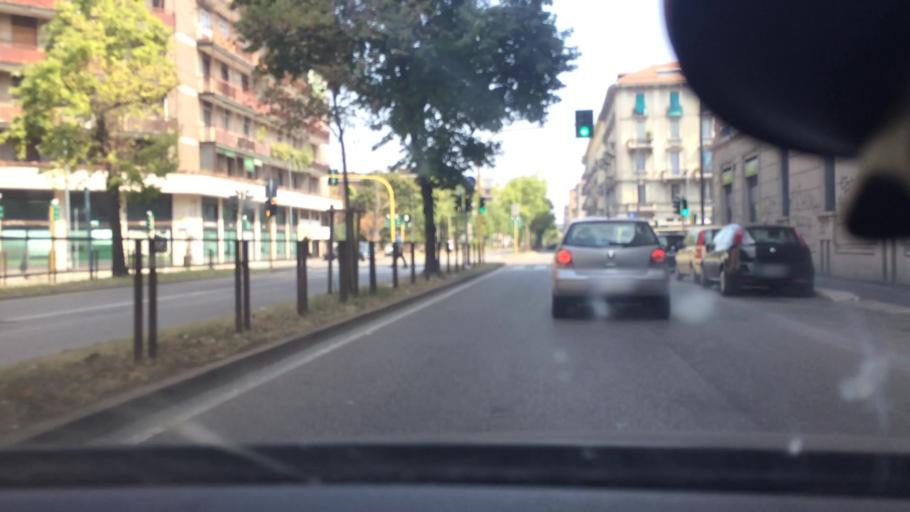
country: IT
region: Lombardy
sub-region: Citta metropolitana di Milano
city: Milano
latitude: 45.4941
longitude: 9.1869
